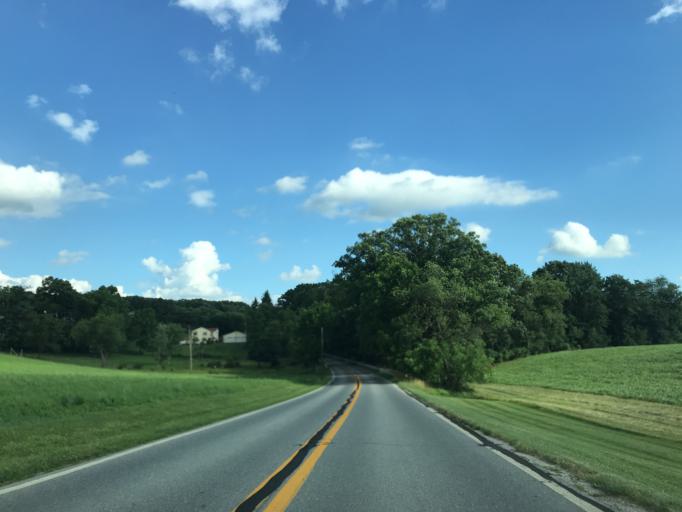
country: US
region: Maryland
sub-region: Carroll County
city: Manchester
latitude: 39.6717
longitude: -76.8206
